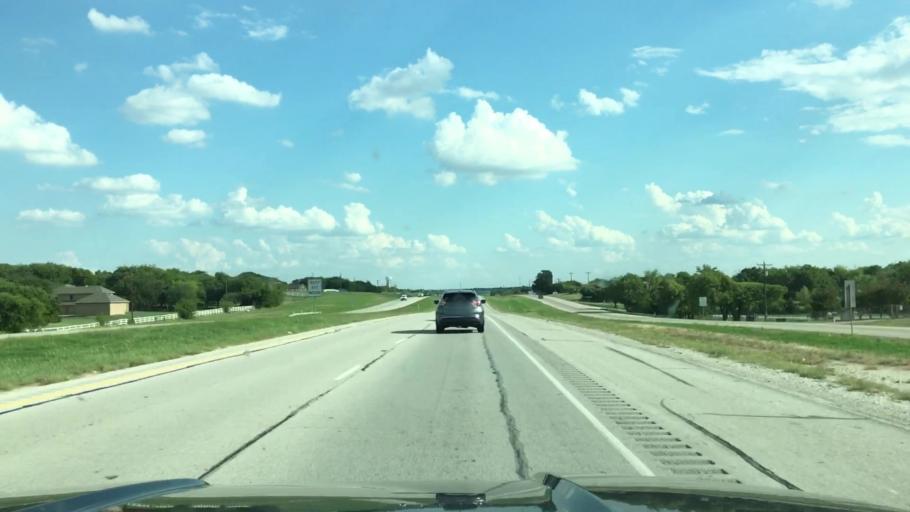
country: US
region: Texas
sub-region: Tarrant County
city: Pecan Acres
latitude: 32.9902
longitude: -97.4302
